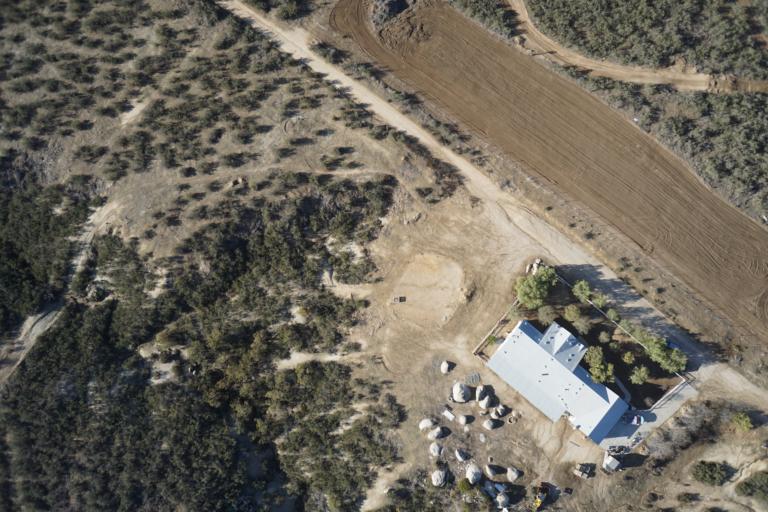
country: US
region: California
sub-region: Riverside County
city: Valle Vista
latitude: 33.6265
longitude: -116.8884
